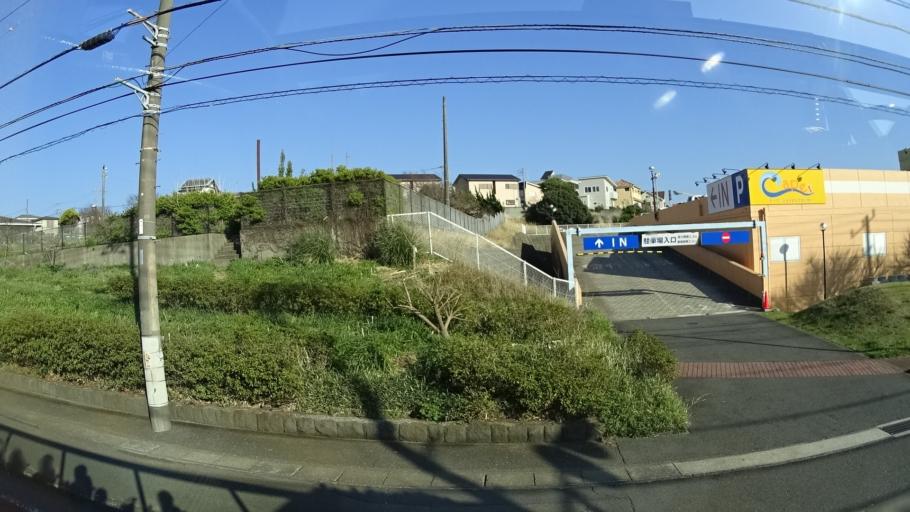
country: JP
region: Kanagawa
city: Miura
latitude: 35.1590
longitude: 139.6388
